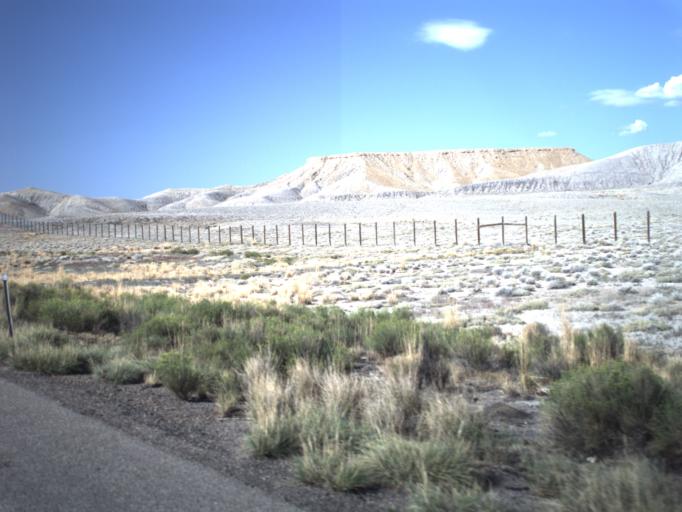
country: US
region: Utah
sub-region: Emery County
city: Huntington
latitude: 39.4248
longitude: -110.8702
